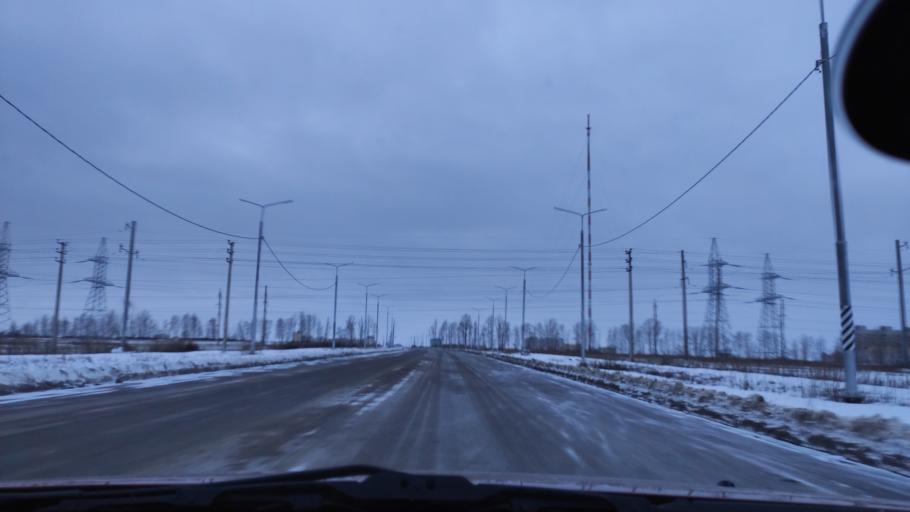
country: RU
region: Tambov
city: Donskoye
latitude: 52.7829
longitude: 41.4287
